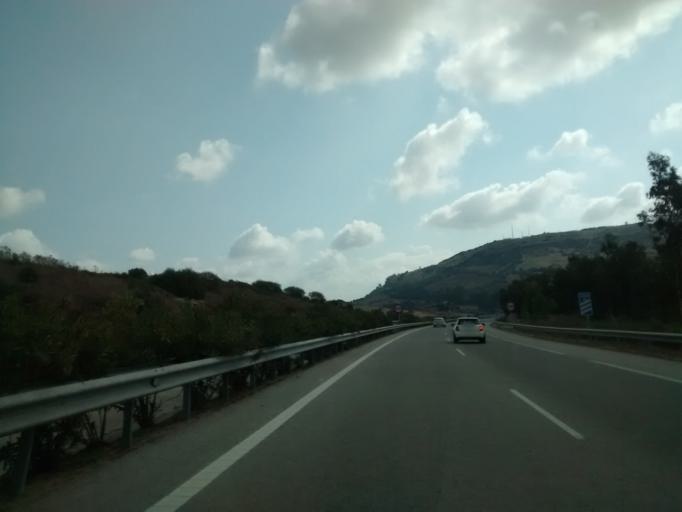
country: ES
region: Andalusia
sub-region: Provincia de Cadiz
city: Vejer de la Frontera
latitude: 36.2537
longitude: -5.9912
